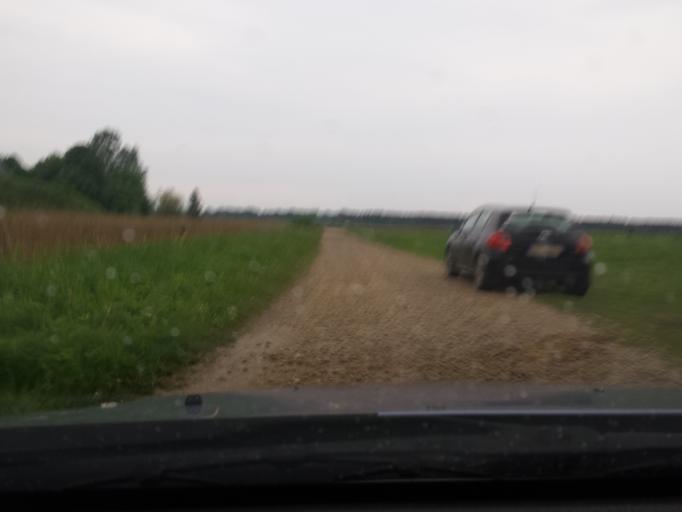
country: LV
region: Riga
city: Bolderaja
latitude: 57.0556
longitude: 24.0944
